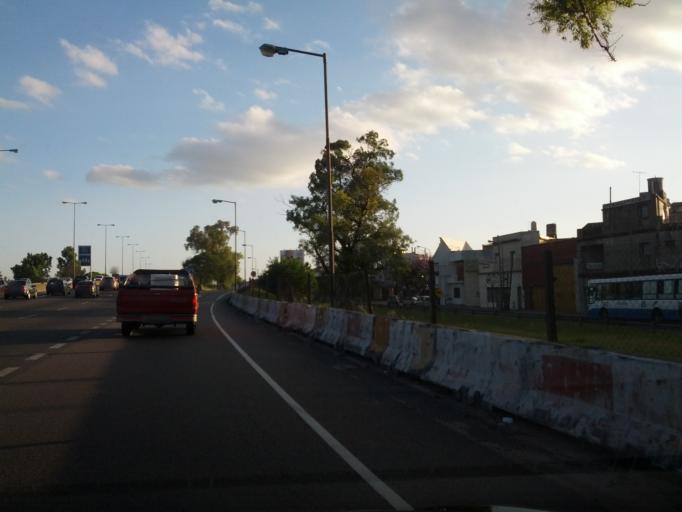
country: AR
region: Buenos Aires
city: San Justo
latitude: -34.6476
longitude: -58.5293
